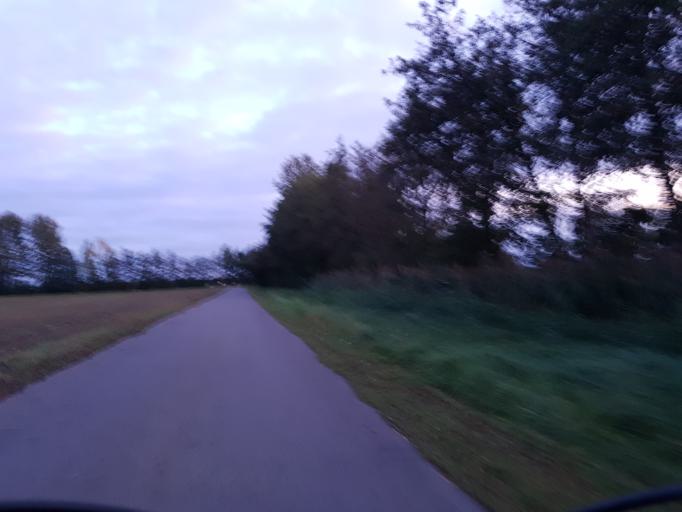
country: DE
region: Brandenburg
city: Schilda
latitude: 51.6245
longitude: 13.3428
